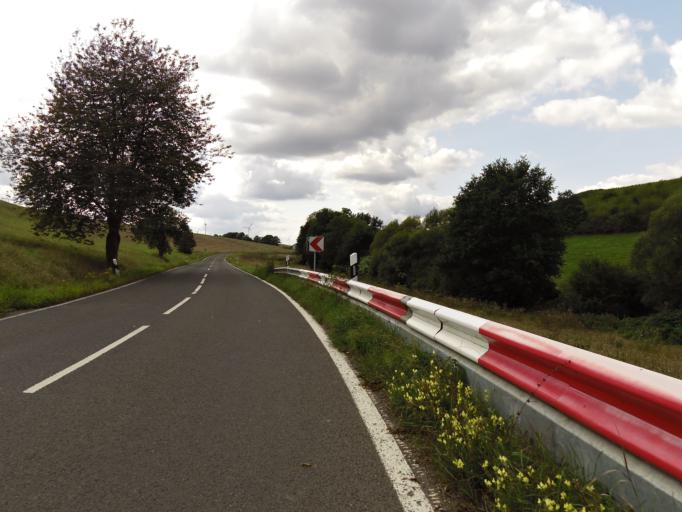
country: DE
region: Rheinland-Pfalz
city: Furfeld
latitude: 49.7755
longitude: 7.9157
